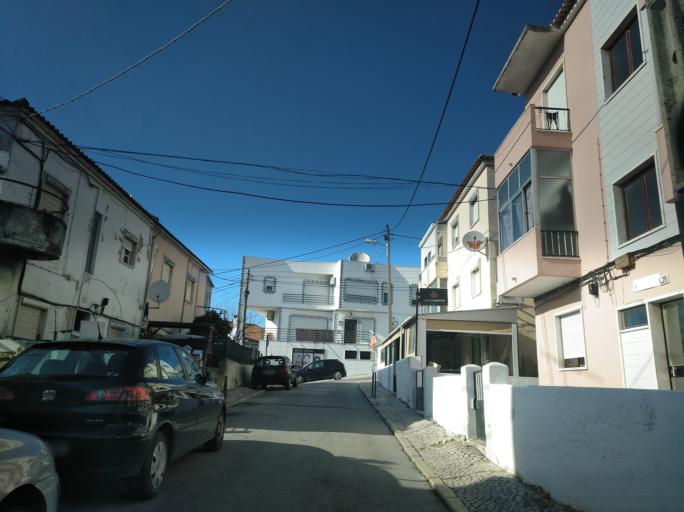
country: PT
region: Lisbon
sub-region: Odivelas
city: Famoes
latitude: 38.7748
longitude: -9.2129
